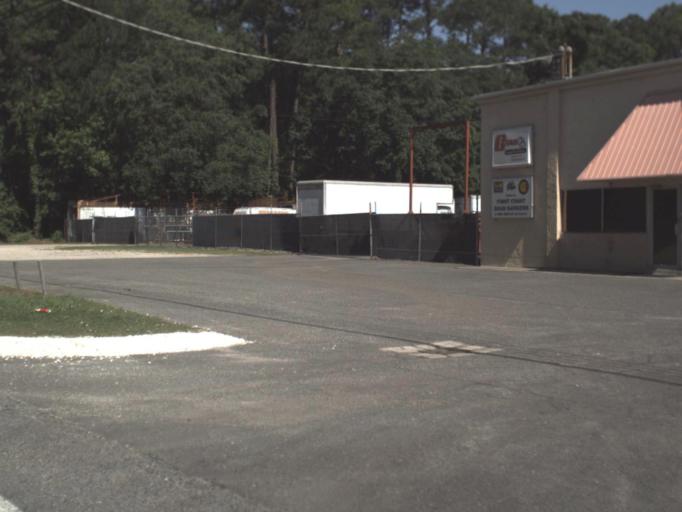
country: US
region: Florida
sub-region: Duval County
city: Jacksonville
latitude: 30.3236
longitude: -81.7591
